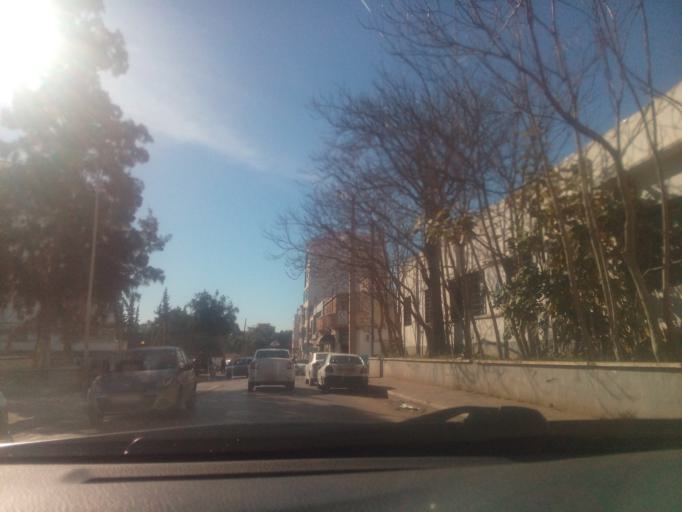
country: DZ
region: Oran
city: Oran
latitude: 35.7035
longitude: -0.6070
